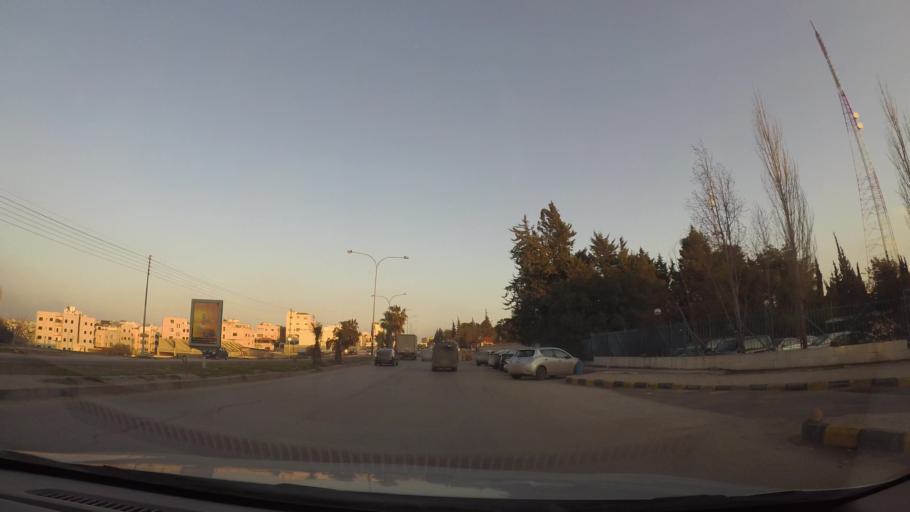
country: JO
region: Amman
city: Al Quwaysimah
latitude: 31.9068
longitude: 35.9322
